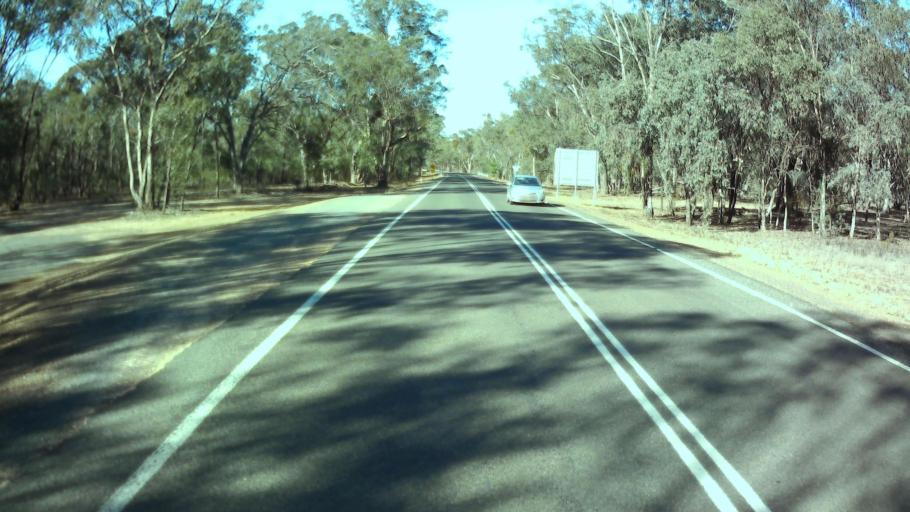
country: AU
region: New South Wales
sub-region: Weddin
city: Grenfell
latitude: -34.0012
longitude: 148.1293
